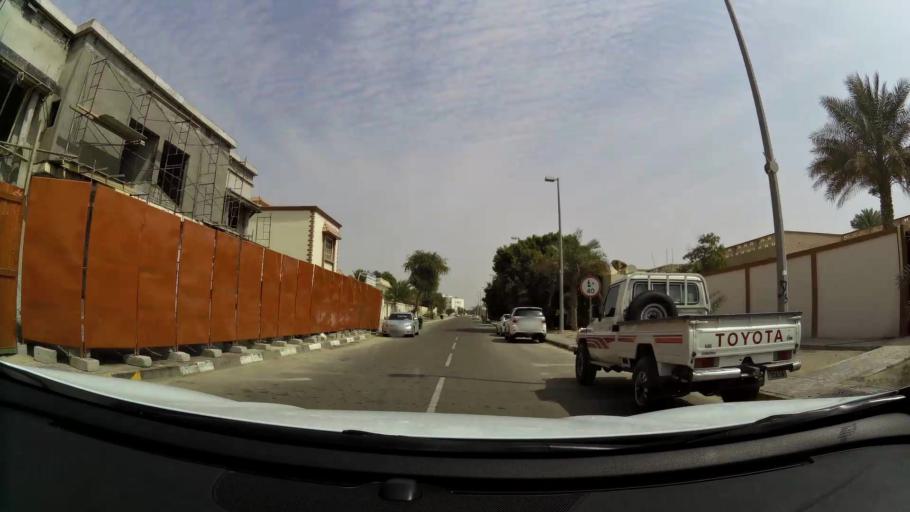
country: AE
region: Abu Dhabi
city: Abu Dhabi
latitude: 24.5316
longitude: 54.6885
